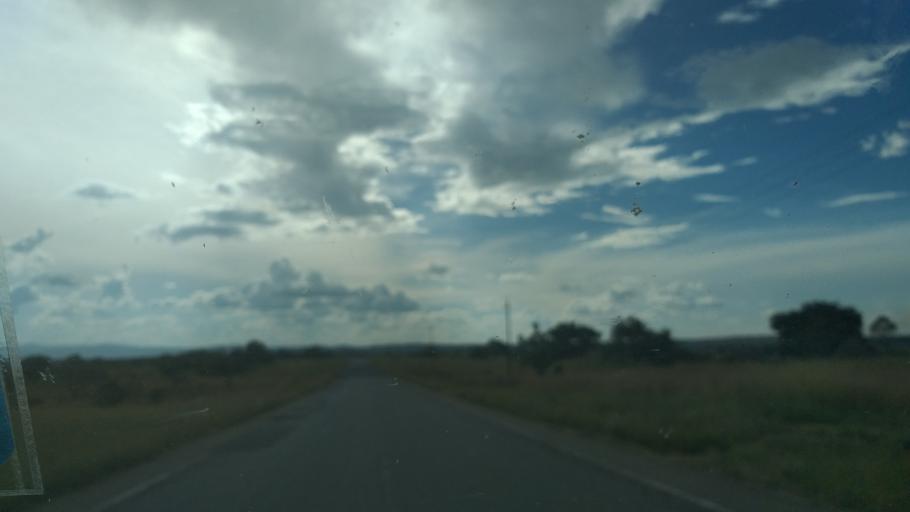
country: UG
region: Northern Region
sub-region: Nebbi District
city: Nebbi
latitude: 2.4605
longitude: 31.2896
